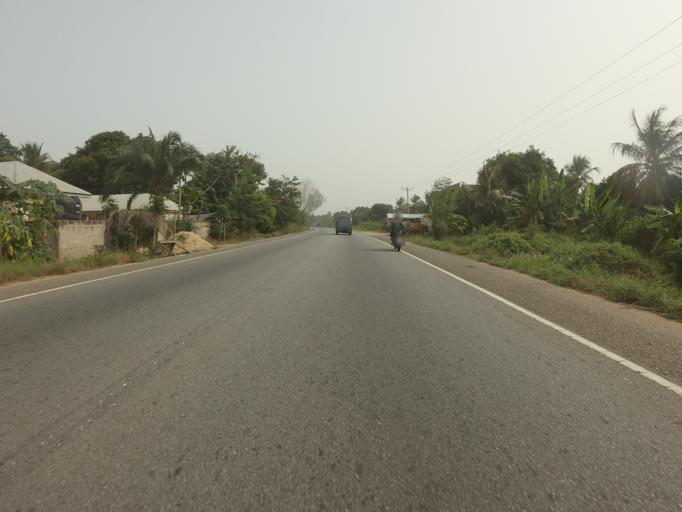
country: GH
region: Volta
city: Anloga
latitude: 5.9951
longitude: 0.5661
